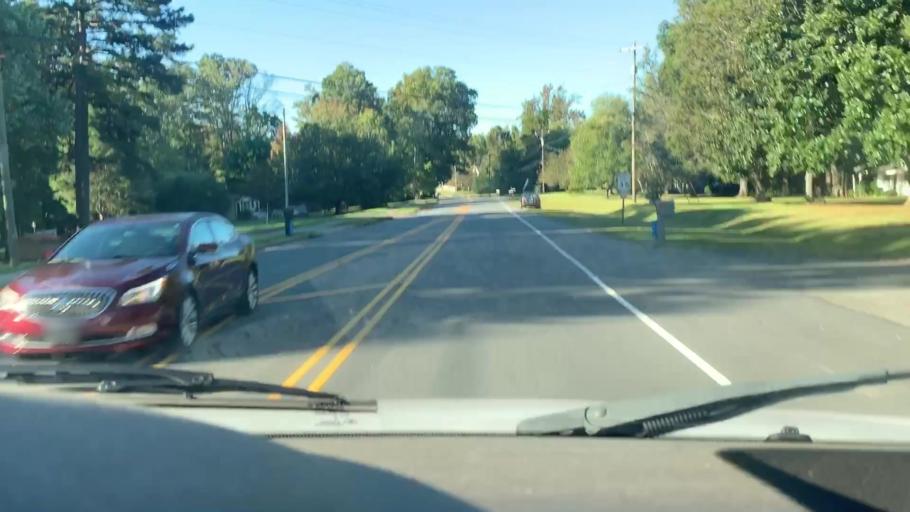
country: US
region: North Carolina
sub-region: Mecklenburg County
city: Charlotte
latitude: 35.2951
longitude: -80.7808
